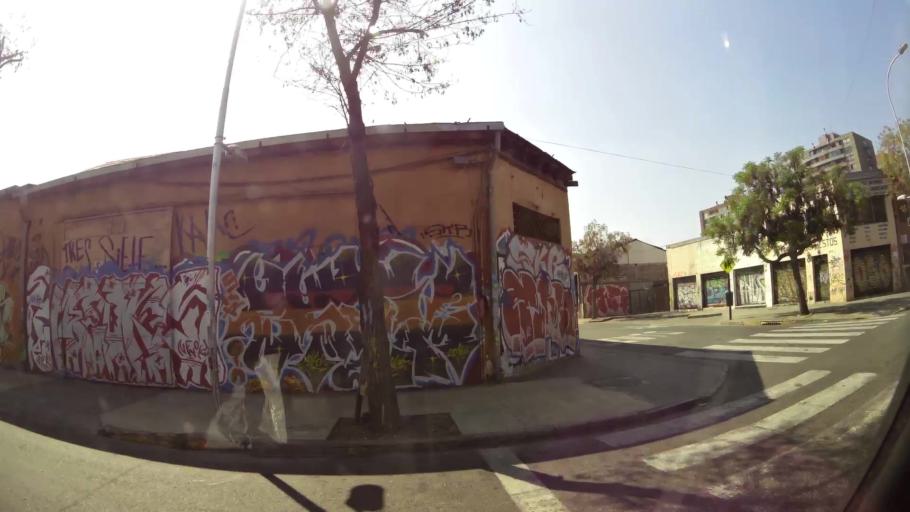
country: CL
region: Santiago Metropolitan
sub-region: Provincia de Santiago
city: Santiago
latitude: -33.4463
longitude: -70.6783
